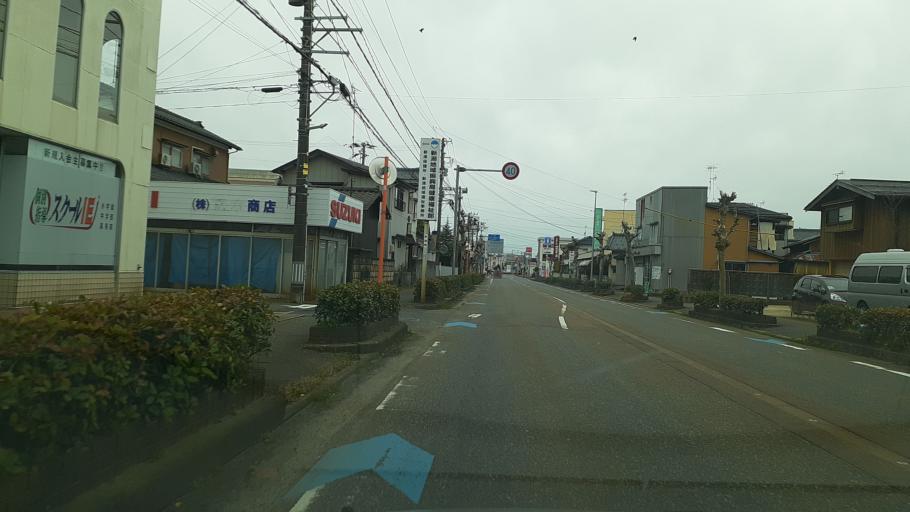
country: JP
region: Niigata
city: Niitsu-honcho
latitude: 37.7946
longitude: 139.1173
